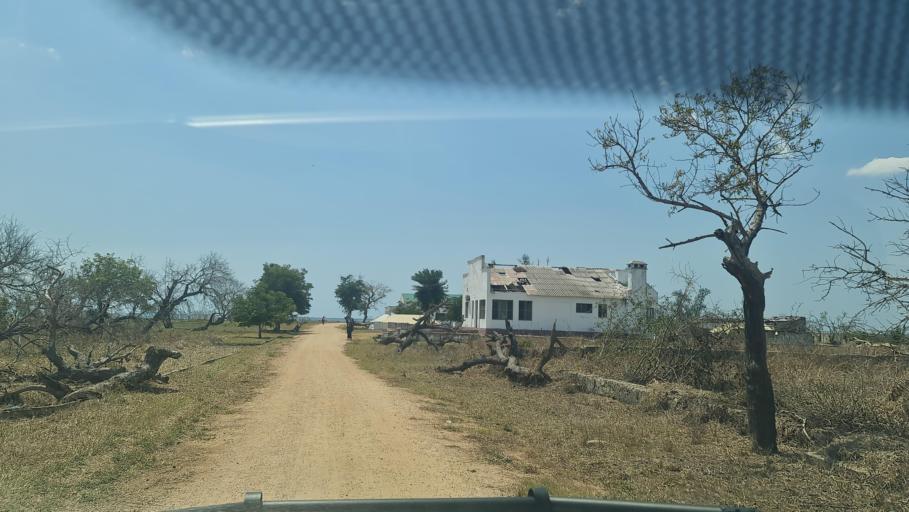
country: MZ
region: Nampula
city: Ilha de Mocambique
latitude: -15.1790
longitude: 40.5130
